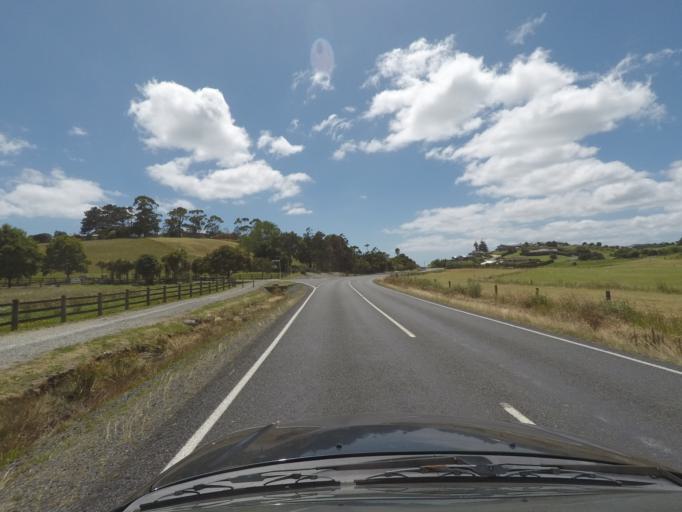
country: NZ
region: Northland
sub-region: Whangarei
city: Ruakaka
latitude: -35.9935
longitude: 174.4647
